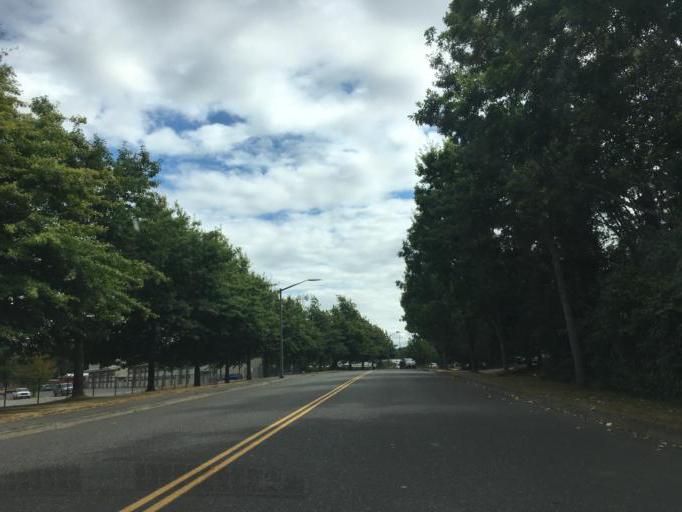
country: US
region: Washington
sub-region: Whatcom County
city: Marietta-Alderwood
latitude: 48.7879
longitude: -122.5290
